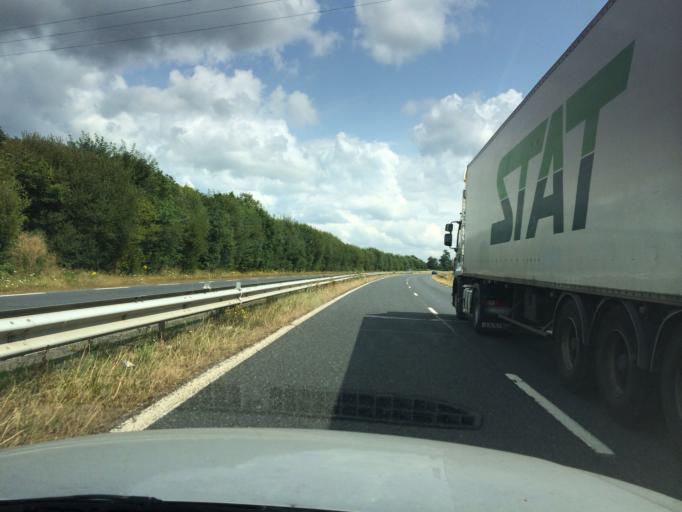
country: FR
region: Lower Normandy
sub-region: Departement du Calvados
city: Grandcamp-Maisy
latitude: 49.3443
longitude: -0.9595
